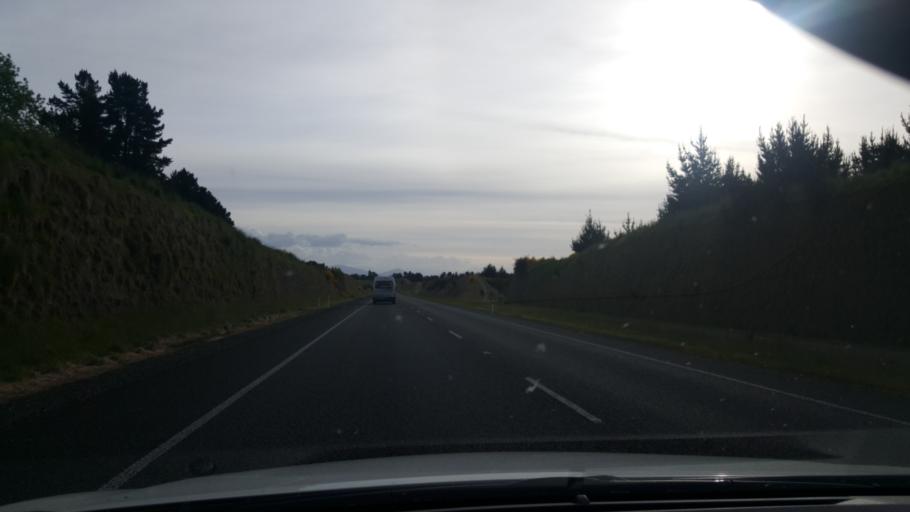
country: NZ
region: Waikato
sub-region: Taupo District
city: Taupo
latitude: -38.7308
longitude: 176.0842
